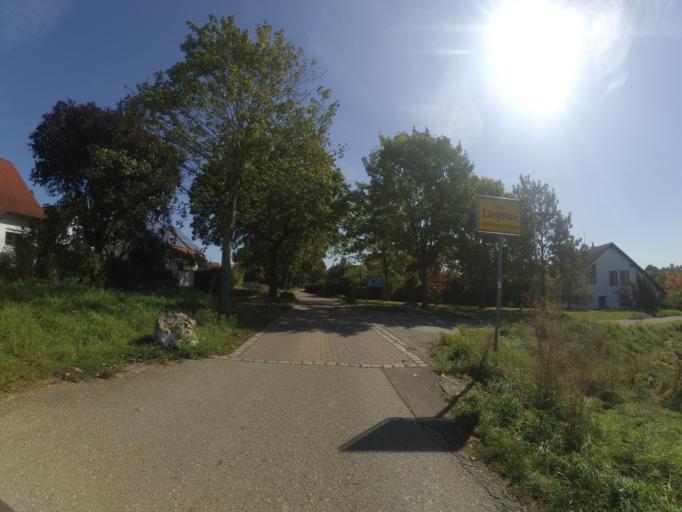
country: DE
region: Baden-Wuerttemberg
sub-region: Tuebingen Region
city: Langenau
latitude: 48.4999
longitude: 10.1067
